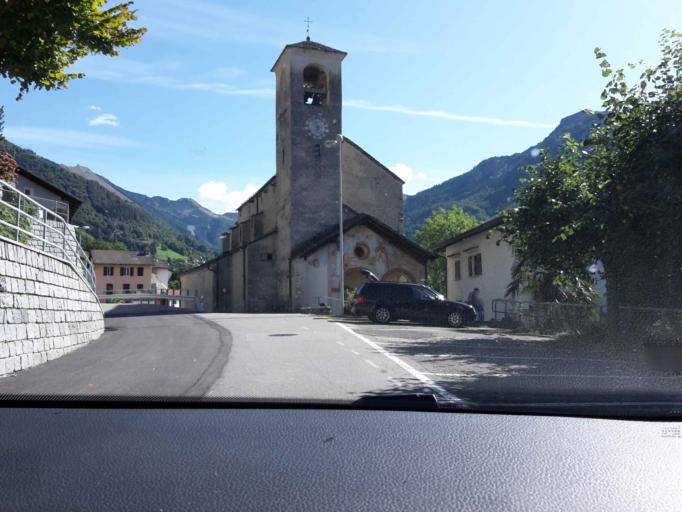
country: CH
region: Ticino
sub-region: Bellinzona District
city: Bellinzona
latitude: 46.1693
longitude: 9.0609
